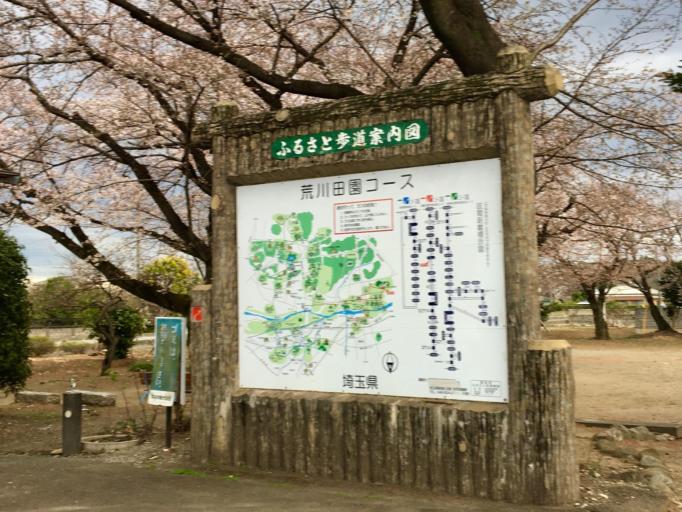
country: JP
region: Saitama
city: Yorii
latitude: 36.1277
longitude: 139.2664
